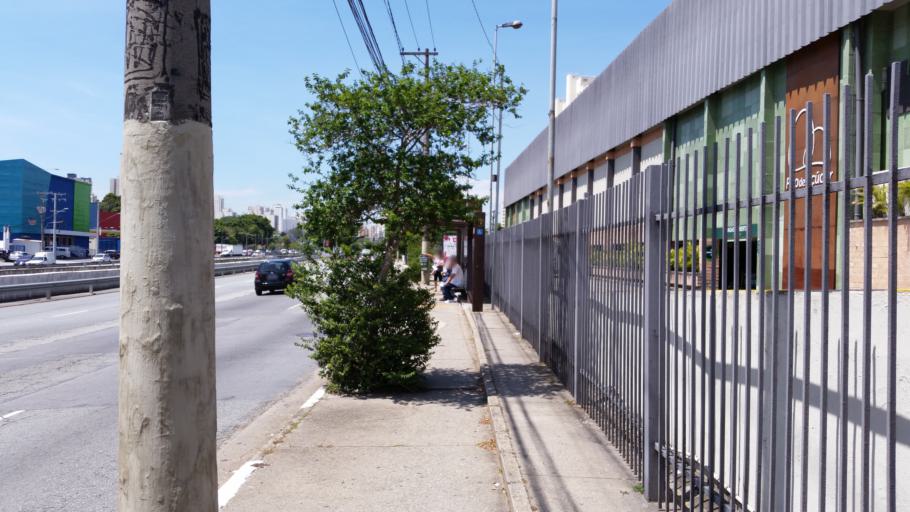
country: BR
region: Sao Paulo
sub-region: Sao Paulo
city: Sao Paulo
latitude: -23.5877
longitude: -46.6199
